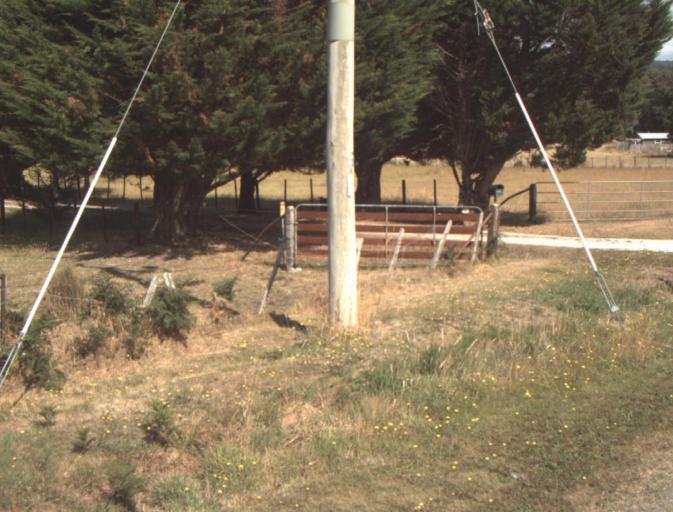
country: AU
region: Tasmania
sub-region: Launceston
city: Mayfield
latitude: -41.2583
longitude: 147.1541
